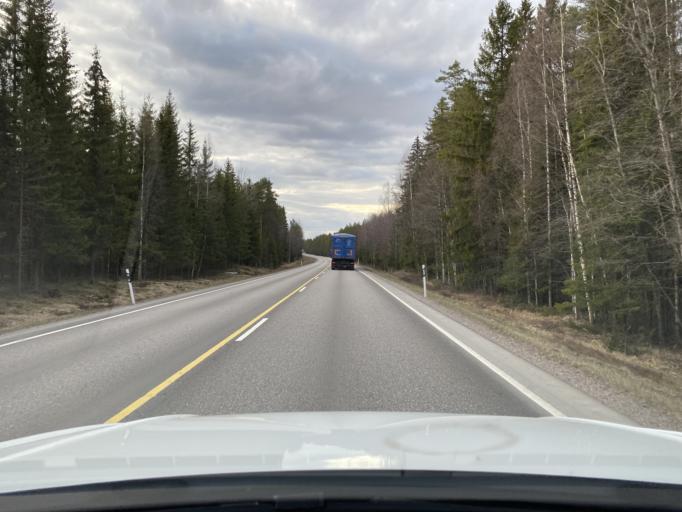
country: FI
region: Uusimaa
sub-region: Helsinki
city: Kaerkoelae
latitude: 60.8071
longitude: 24.0667
